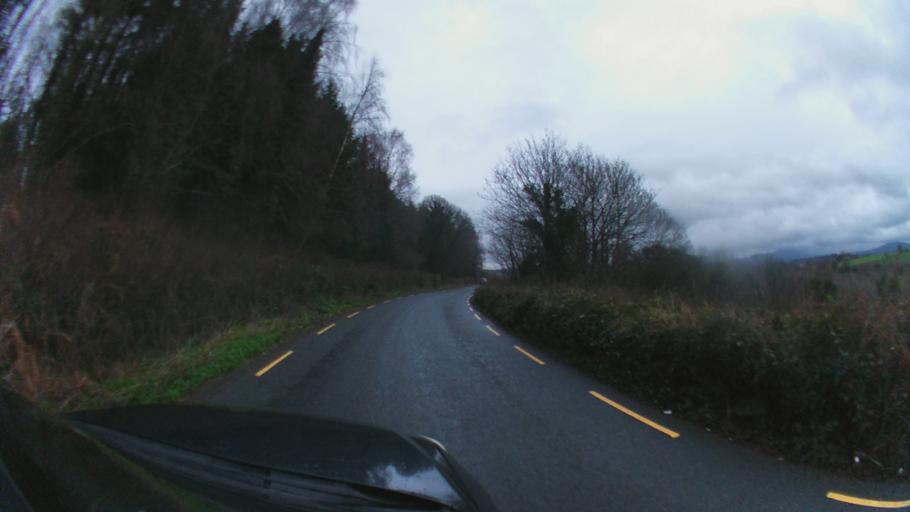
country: IE
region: Leinster
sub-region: Kilkenny
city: Graiguenamanagh
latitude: 52.5810
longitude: -6.9532
